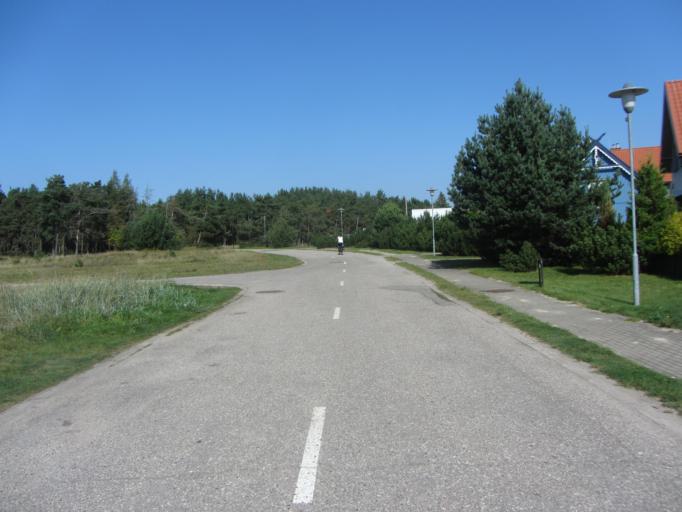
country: LT
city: Neringa
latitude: 55.3760
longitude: 21.0695
